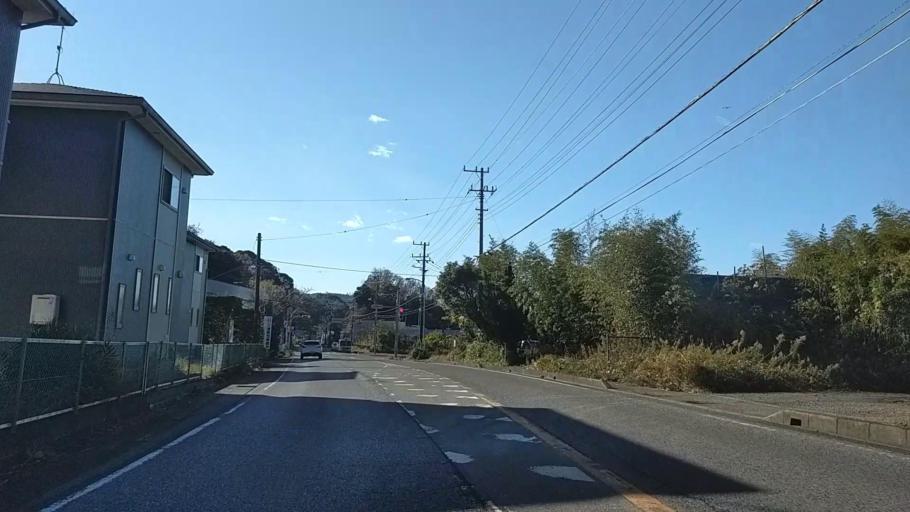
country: JP
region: Chiba
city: Futtsu
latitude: 35.2274
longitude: 139.8739
